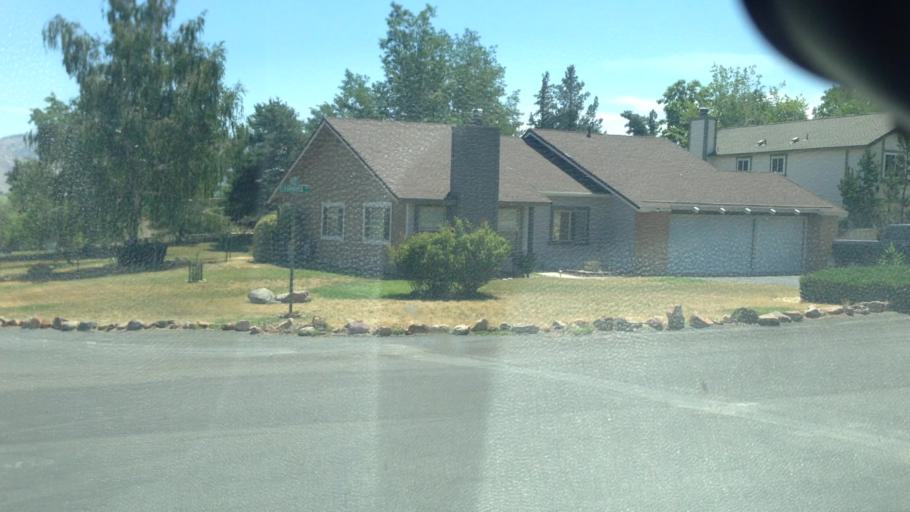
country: US
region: Nevada
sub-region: Washoe County
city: Sparks
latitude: 39.4217
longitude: -119.7676
